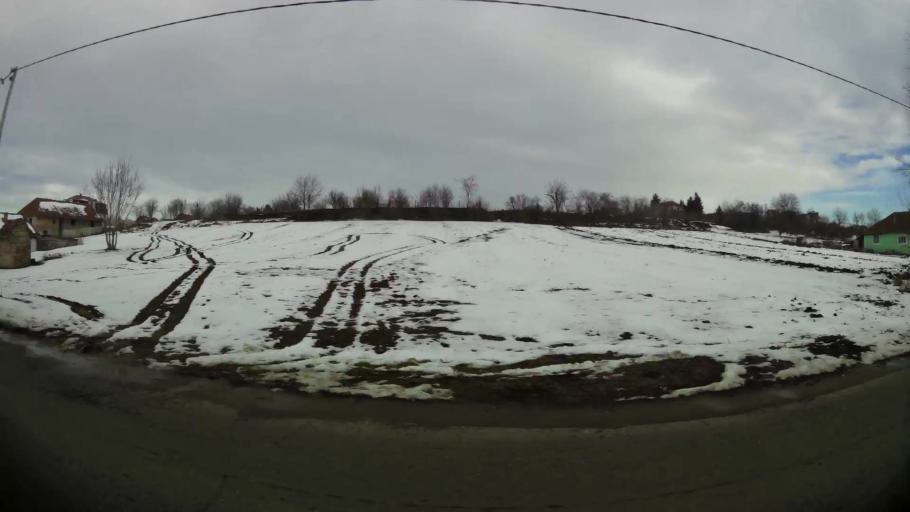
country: RS
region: Central Serbia
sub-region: Belgrade
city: Surcin
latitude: 44.7892
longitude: 20.2832
